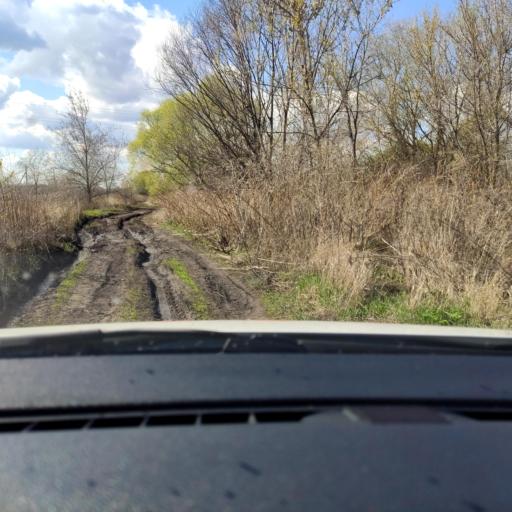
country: RU
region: Voronezj
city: Pridonskoy
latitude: 51.6967
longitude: 39.0532
